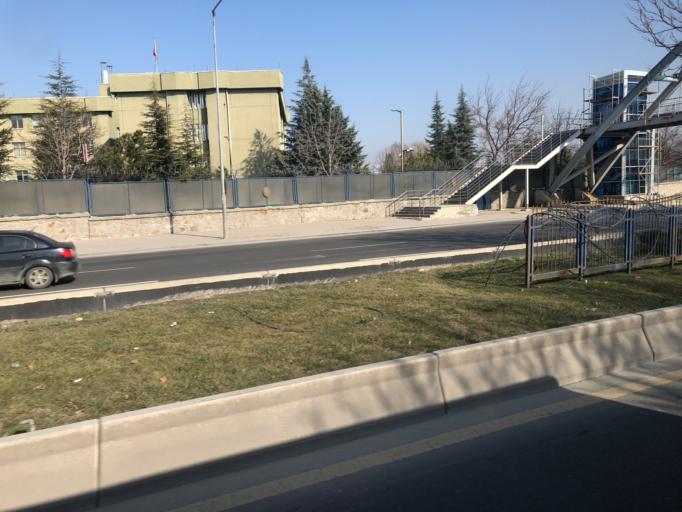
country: TR
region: Ankara
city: Ankara
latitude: 39.9619
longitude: 32.8452
